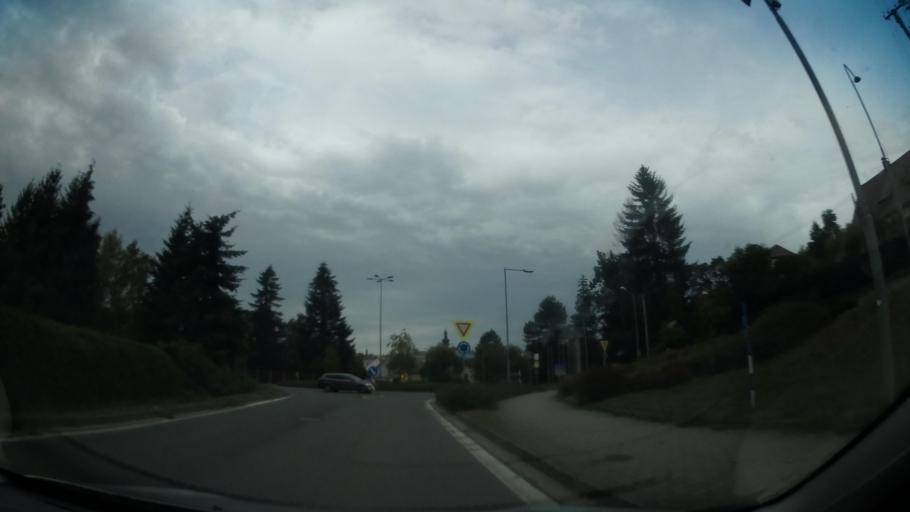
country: CZ
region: Vysocina
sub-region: Okres Zd'ar nad Sazavou
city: Nove Mesto na Morave
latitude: 49.5571
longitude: 16.0730
